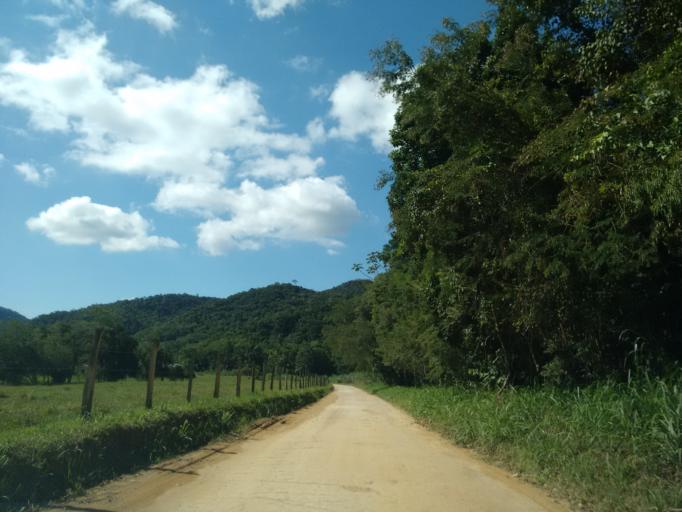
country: BR
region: Santa Catarina
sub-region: Indaial
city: Indaial
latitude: -26.9601
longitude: -49.1781
